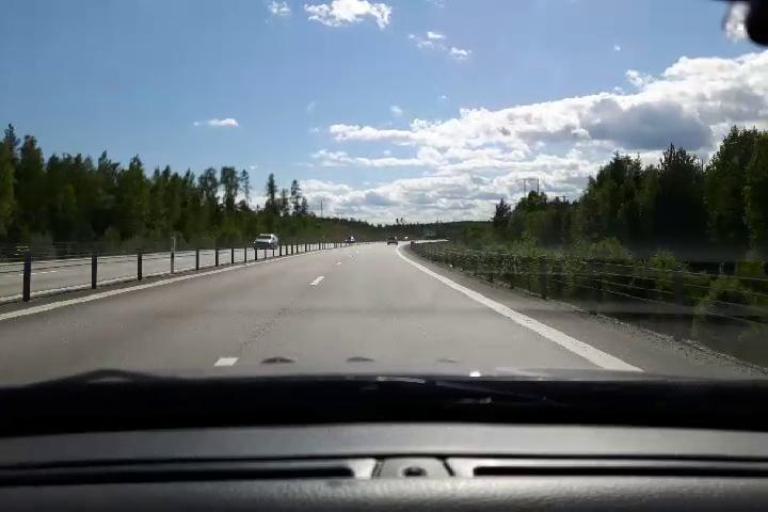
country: SE
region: Gaevleborg
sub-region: Hudiksvalls Kommun
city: Iggesund
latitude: 61.6887
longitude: 17.0532
